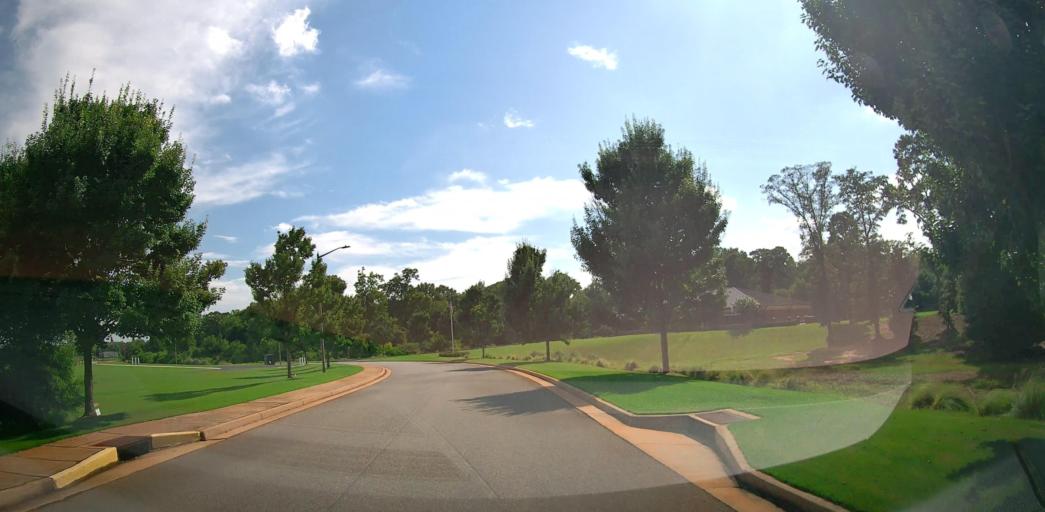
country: US
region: Georgia
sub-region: Houston County
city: Centerville
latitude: 32.5417
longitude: -83.6773
